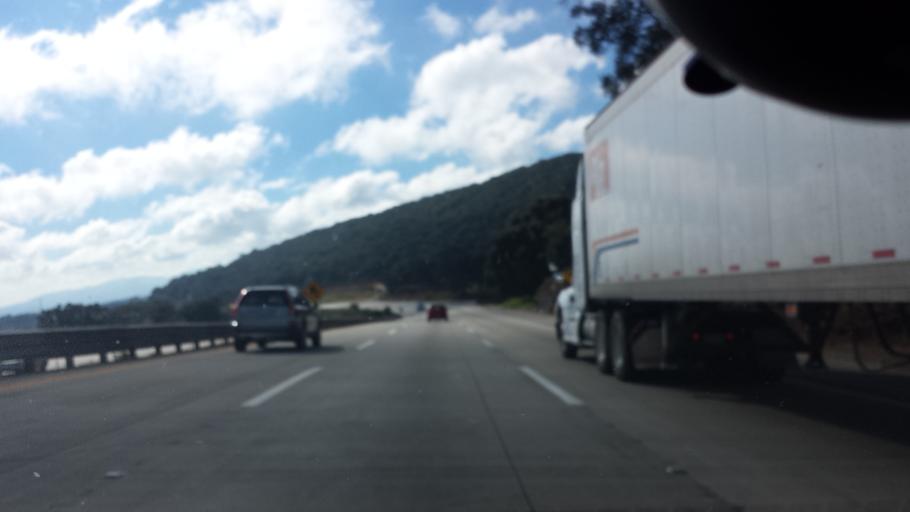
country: MX
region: Mexico
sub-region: Jilotepec
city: San Vicente (Calpulalpan Tercera Manzana)
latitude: 20.0683
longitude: -99.6032
